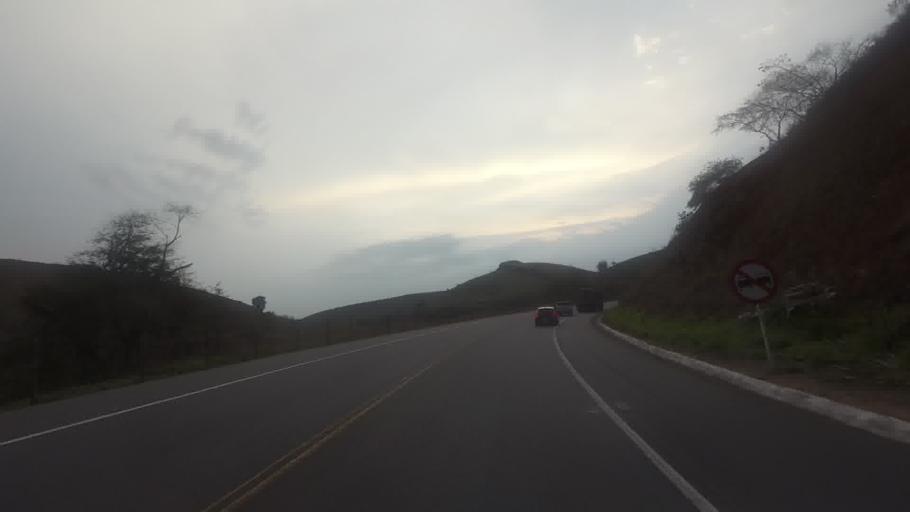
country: BR
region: Rio de Janeiro
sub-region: Carmo
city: Carmo
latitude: -21.8115
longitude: -42.5897
